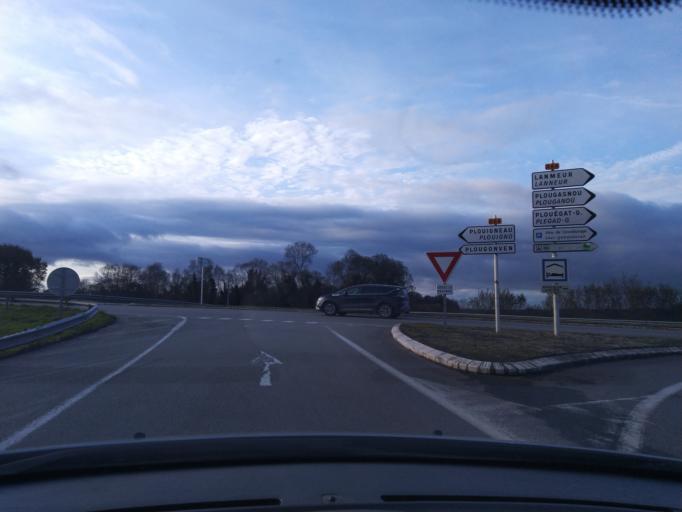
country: FR
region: Brittany
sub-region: Departement du Finistere
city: Plouigneau
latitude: 48.5757
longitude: -3.7170
